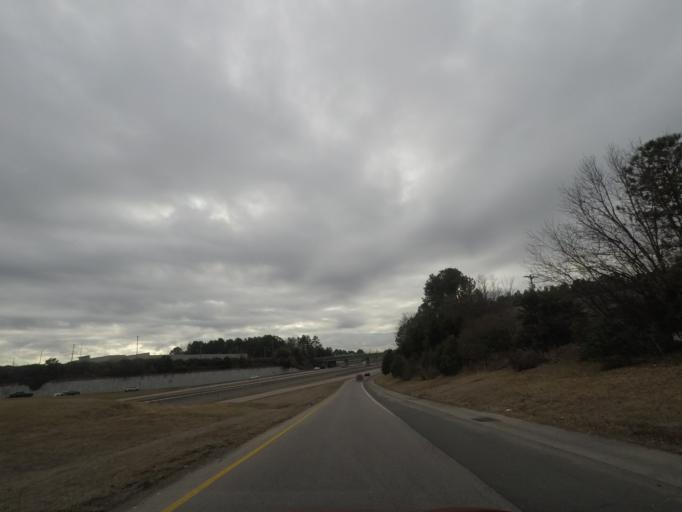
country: US
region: North Carolina
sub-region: Durham County
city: Durham
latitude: 36.0206
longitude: -78.9501
